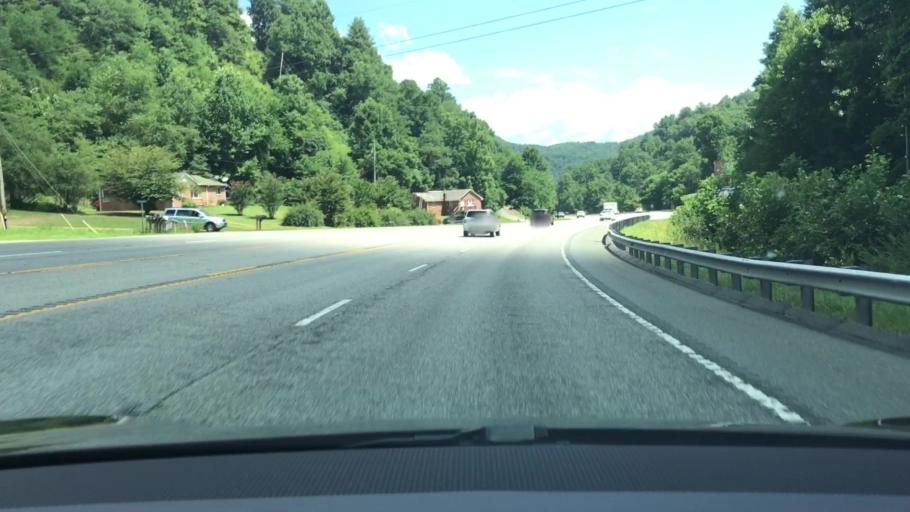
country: US
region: North Carolina
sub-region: Jackson County
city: Sylva
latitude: 35.2785
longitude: -83.2883
